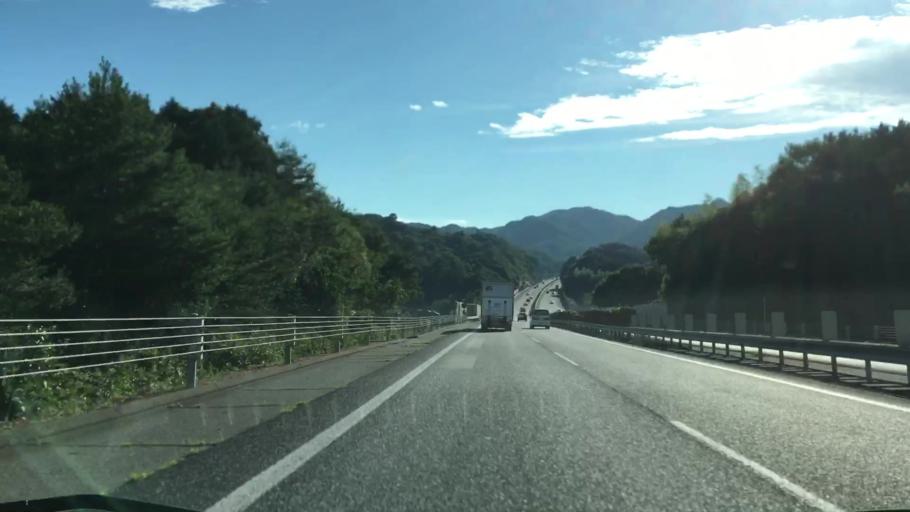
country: JP
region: Yamaguchi
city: Yanai
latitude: 34.0678
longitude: 132.0588
